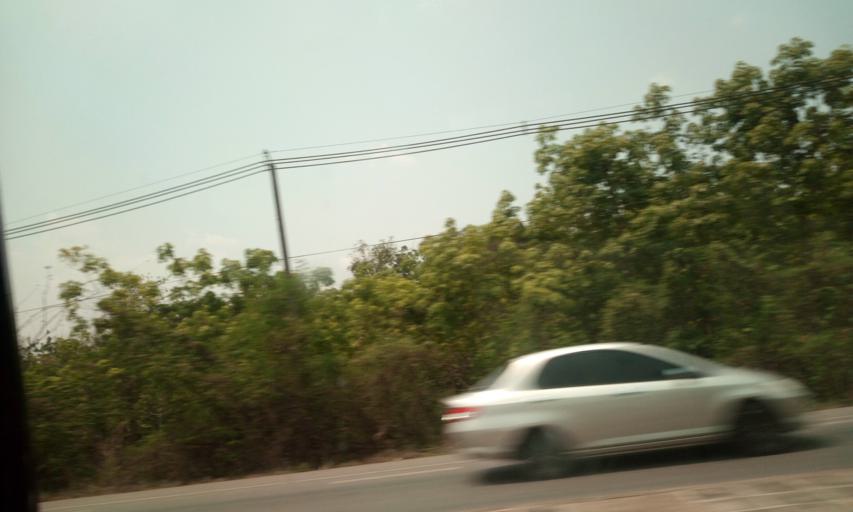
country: TH
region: Chiang Rai
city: Pa Daet
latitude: 19.6014
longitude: 100.0508
